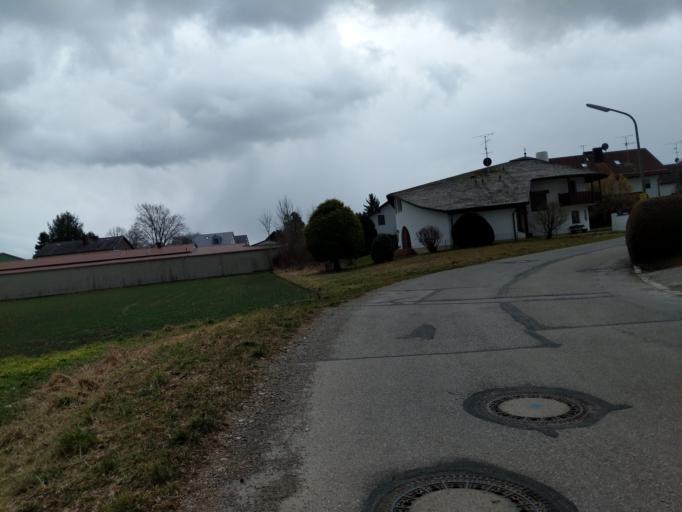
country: DE
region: Bavaria
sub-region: Upper Bavaria
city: Zorneding
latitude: 48.0952
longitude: 11.8353
